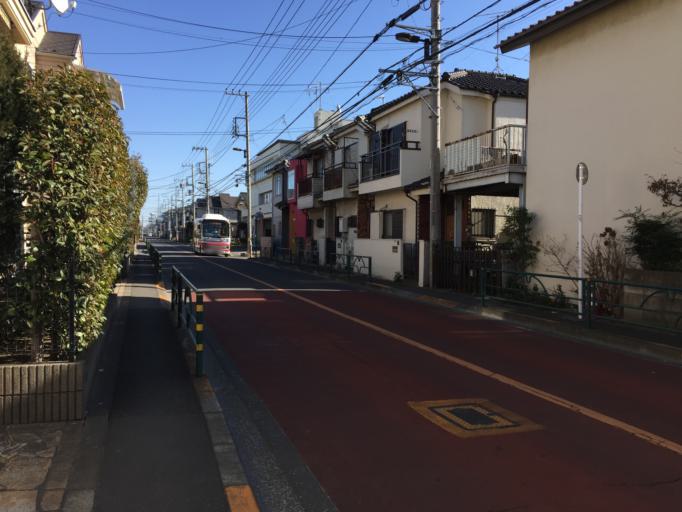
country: JP
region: Tokyo
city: Chofugaoka
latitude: 35.6275
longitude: 139.5838
